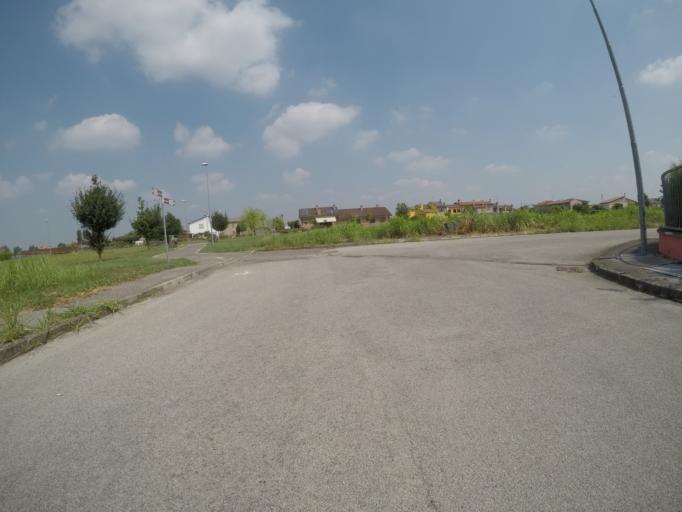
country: IT
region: Veneto
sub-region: Provincia di Rovigo
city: Villanova del Ghebbo Canton
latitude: 45.0574
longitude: 11.6391
